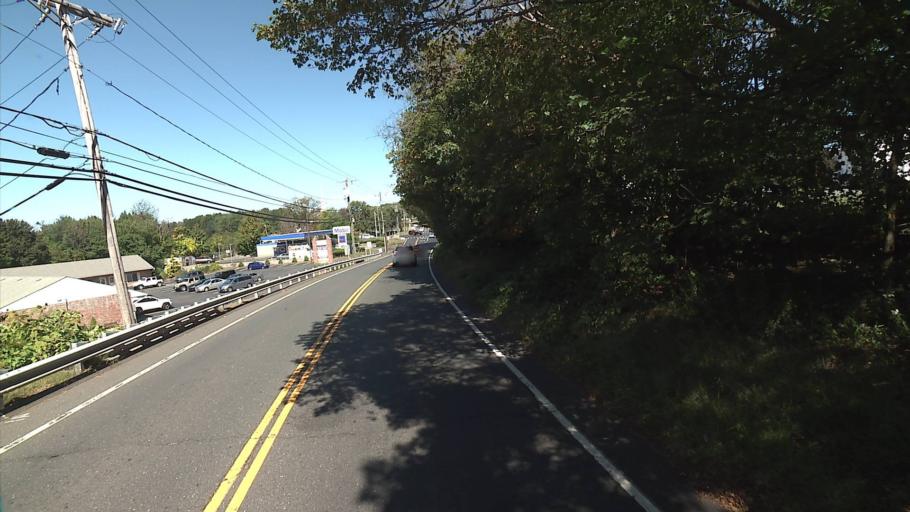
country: US
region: Connecticut
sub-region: New Haven County
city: Prospect
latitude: 41.5011
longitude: -72.9790
